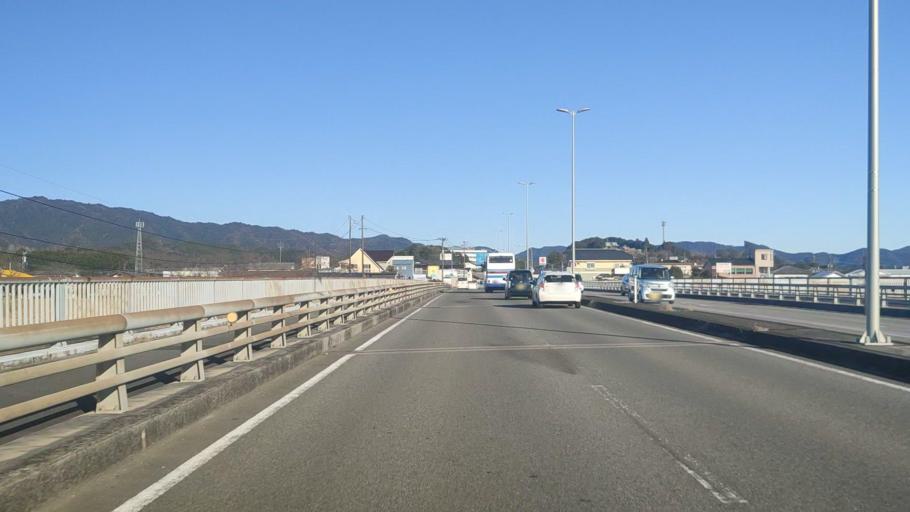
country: JP
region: Miyazaki
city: Nobeoka
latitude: 32.4640
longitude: 131.6486
